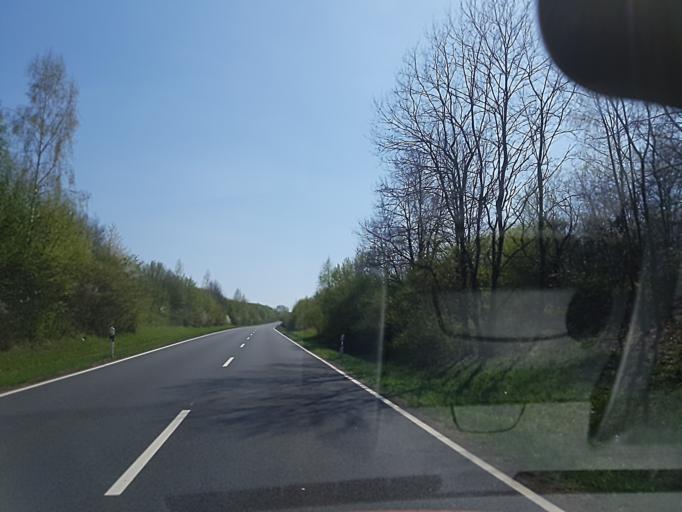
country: DE
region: Saxony
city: Leisnig
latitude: 51.1655
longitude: 12.9074
